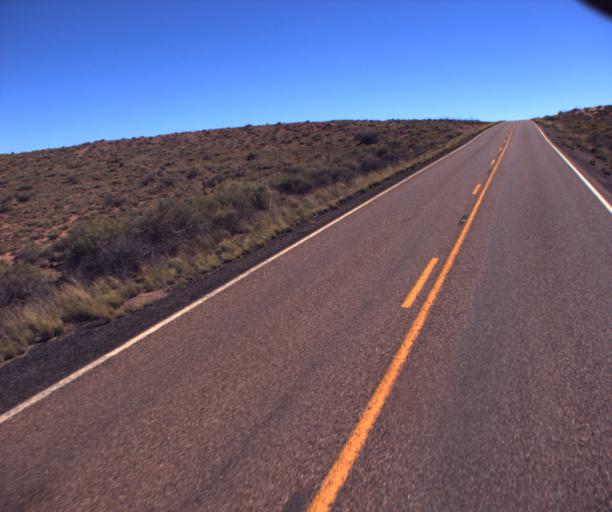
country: US
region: Arizona
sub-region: Navajo County
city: Holbrook
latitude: 35.0489
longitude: -110.0946
